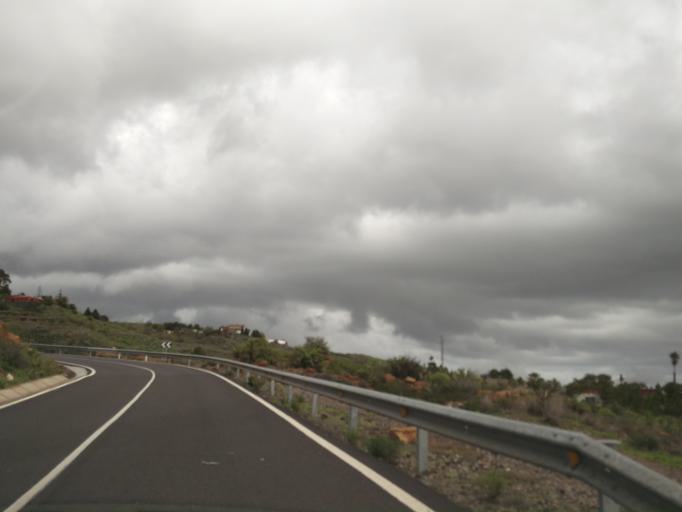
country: ES
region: Canary Islands
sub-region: Provincia de Santa Cruz de Tenerife
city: Arona
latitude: 28.1084
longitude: -16.6855
